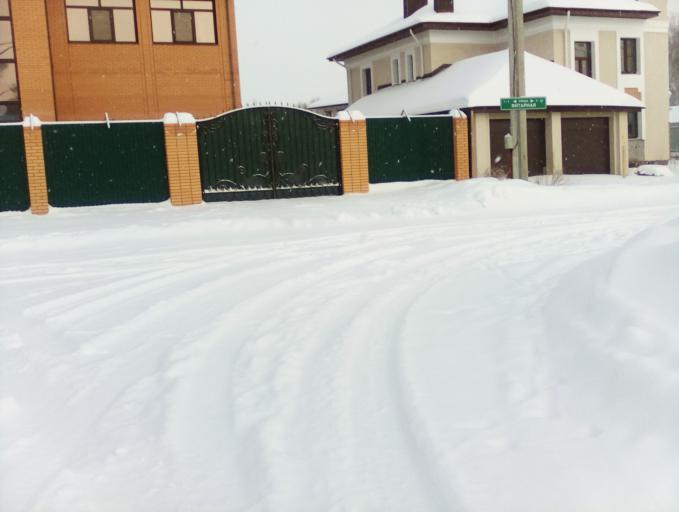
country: RU
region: Chelyabinsk
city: Poletayevo
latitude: 55.1552
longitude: 61.1400
